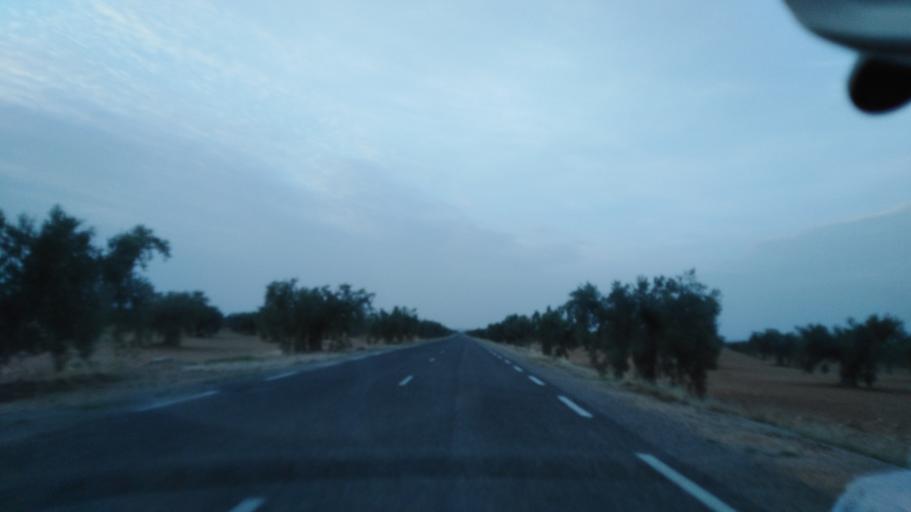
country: TN
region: Safaqis
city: Bi'r `Ali Bin Khalifah
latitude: 34.9196
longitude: 10.3873
